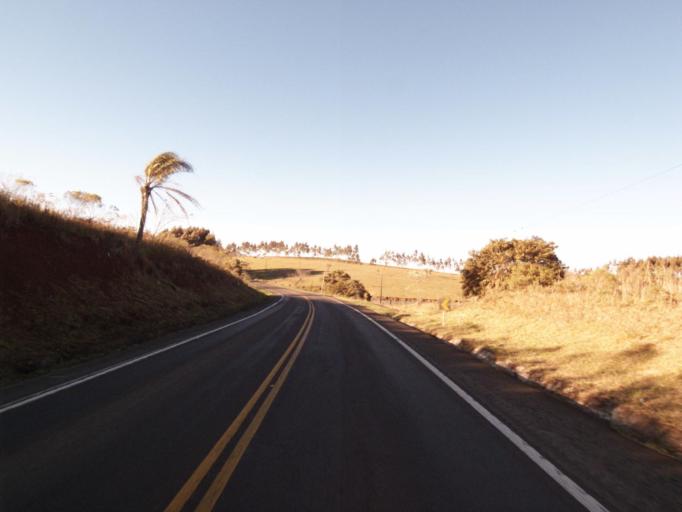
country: AR
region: Misiones
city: Bernardo de Irigoyen
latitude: -26.3027
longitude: -53.5525
